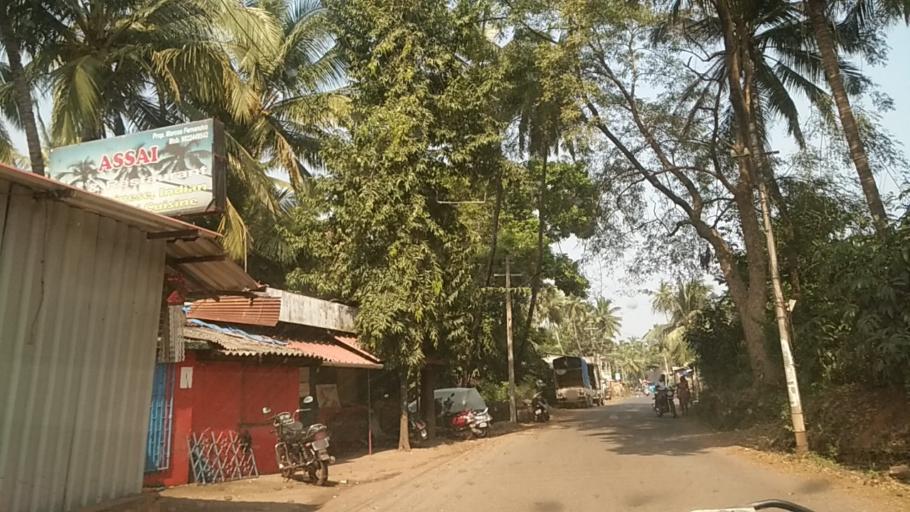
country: IN
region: Goa
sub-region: South Goa
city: Cavelossim
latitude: 15.1456
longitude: 73.9557
